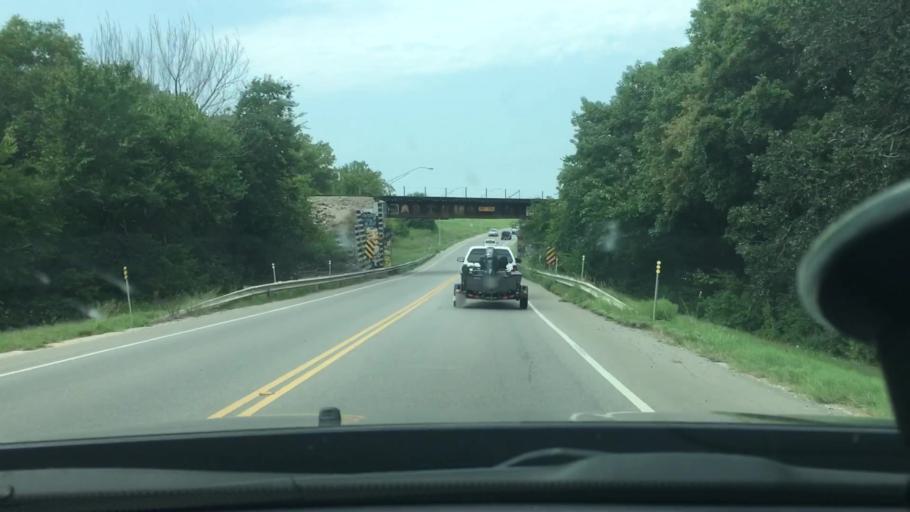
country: US
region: Oklahoma
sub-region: Marshall County
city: Madill
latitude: 34.0625
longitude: -96.7565
